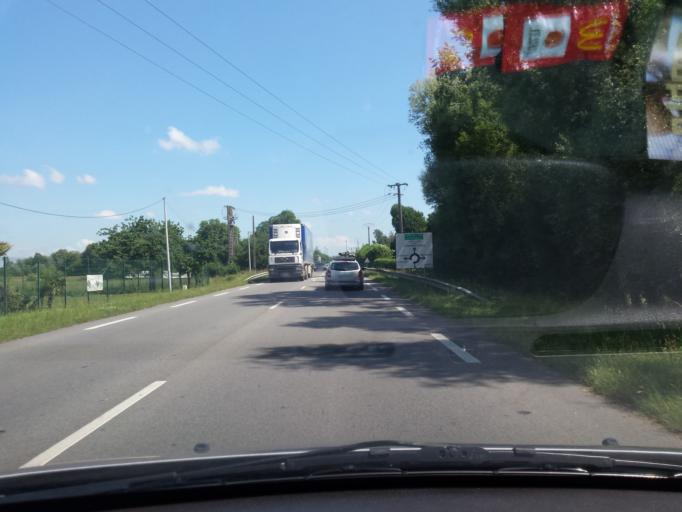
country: FR
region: Pays de la Loire
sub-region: Departement de la Loire-Atlantique
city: Machecoul
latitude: 46.9962
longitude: -1.8098
